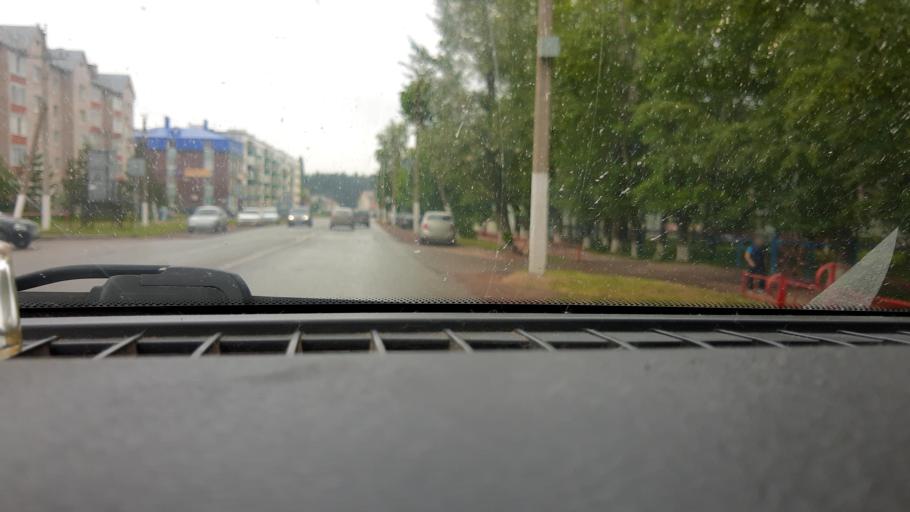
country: RU
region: Bashkortostan
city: Belebey
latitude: 54.1058
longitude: 54.0963
